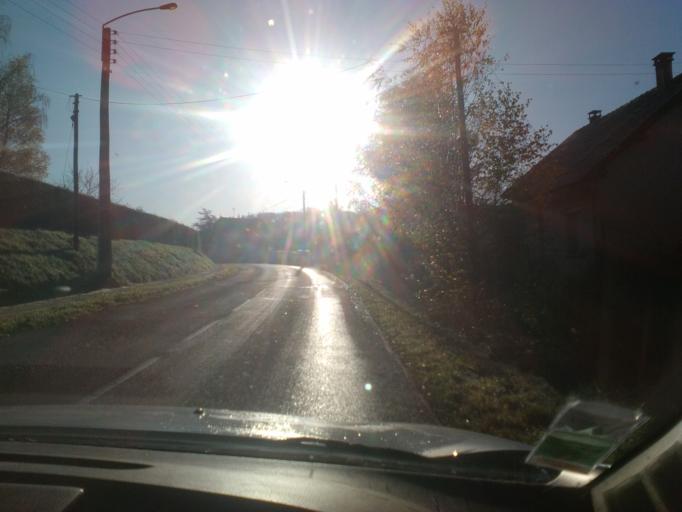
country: FR
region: Lorraine
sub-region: Departement des Vosges
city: Xertigny
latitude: 48.0535
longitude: 6.3734
